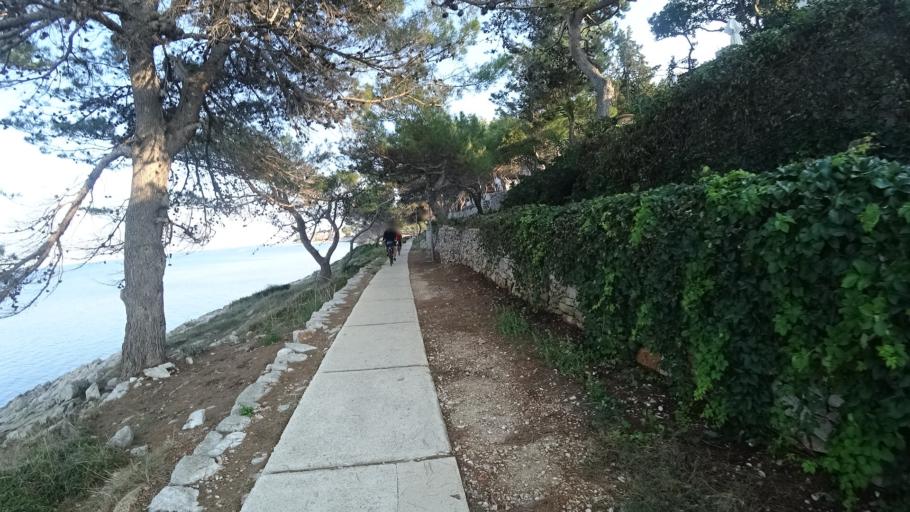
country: HR
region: Primorsko-Goranska
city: Mali Losinj
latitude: 44.5277
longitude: 14.4878
